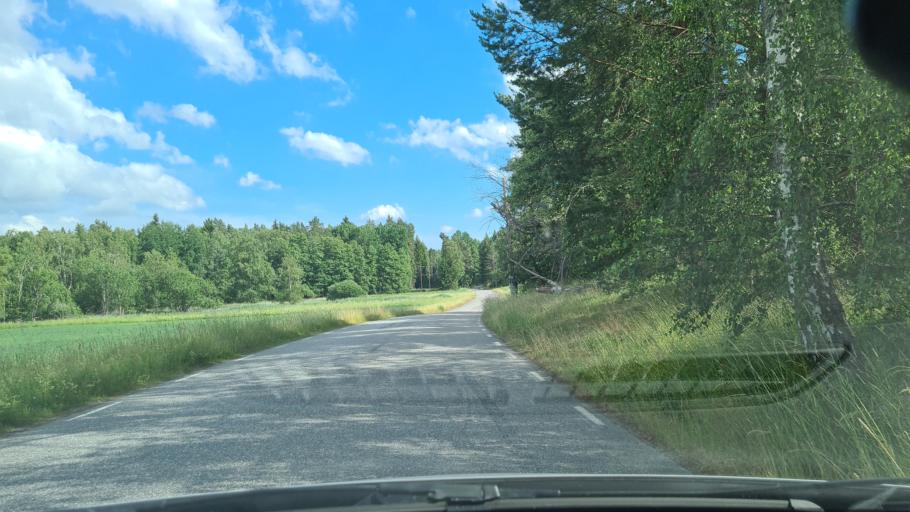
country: SE
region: Stockholm
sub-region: Varmdo Kommun
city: Mortnas
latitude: 59.4066
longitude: 18.4569
